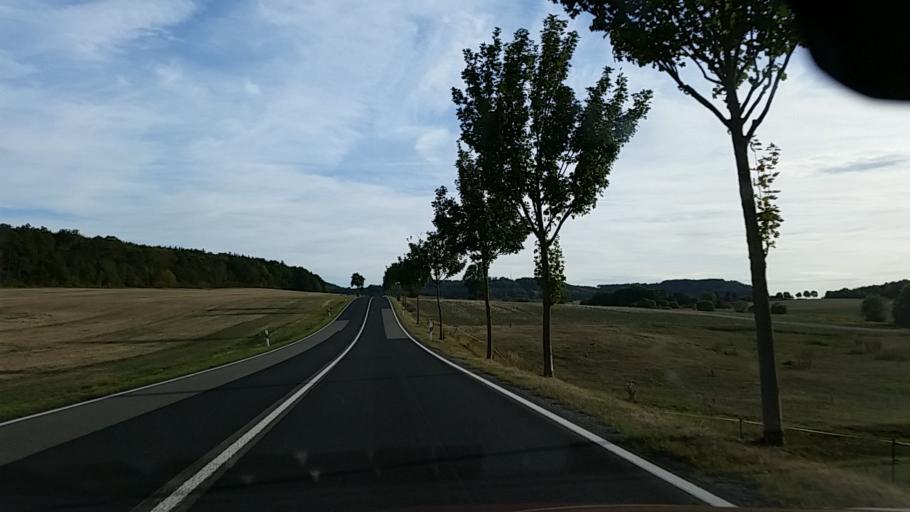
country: DE
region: Thuringia
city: Henneberg
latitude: 50.5099
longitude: 10.3577
